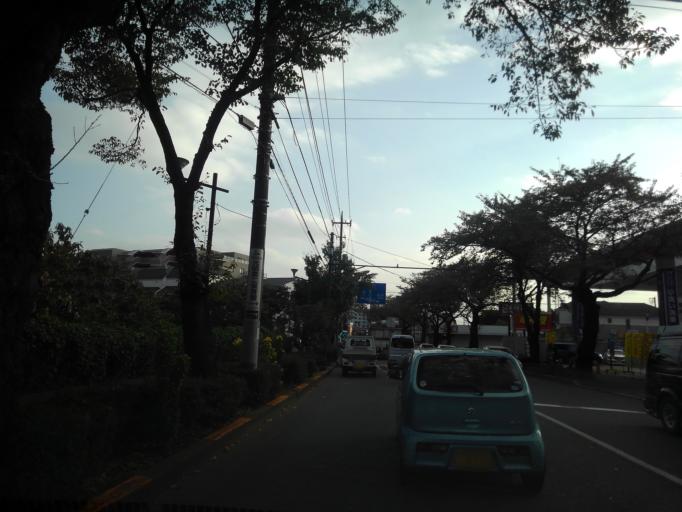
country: JP
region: Tokyo
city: Kokubunji
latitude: 35.6908
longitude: 139.4981
